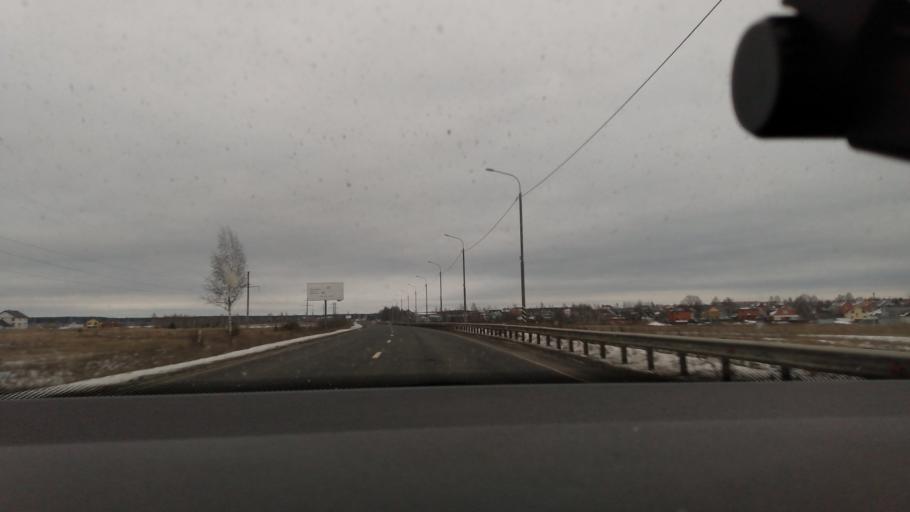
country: RU
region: Moskovskaya
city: Yegor'yevsk
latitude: 55.3972
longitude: 39.0646
